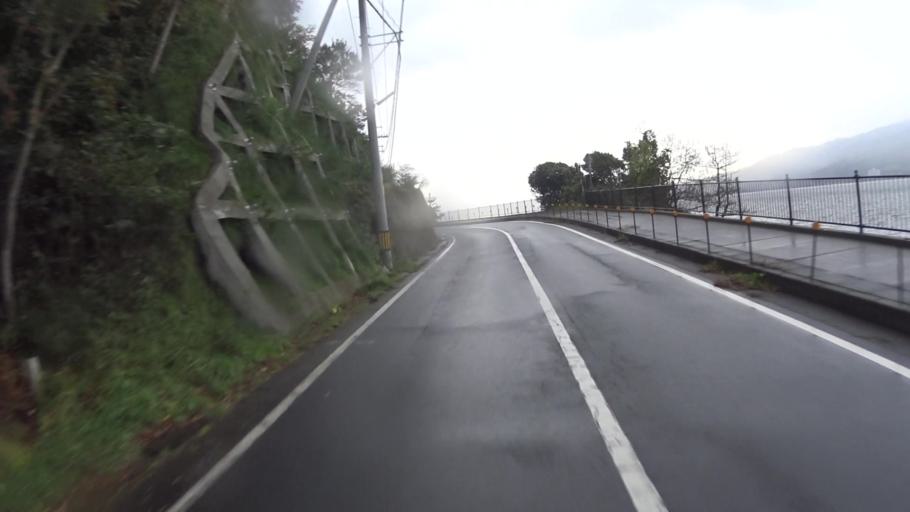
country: JP
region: Kyoto
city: Miyazu
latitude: 35.5754
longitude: 135.2296
